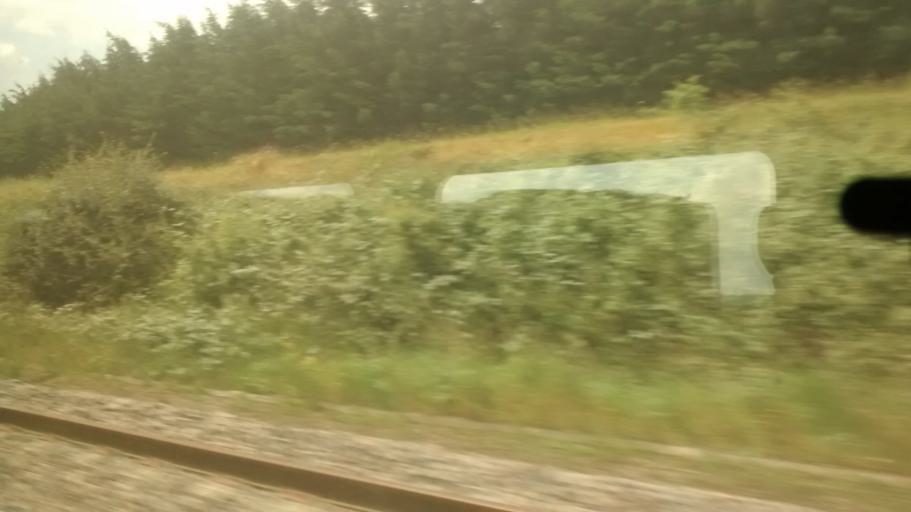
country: FR
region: Bourgogne
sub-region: Departement de Saone-et-Loire
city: Epinac
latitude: 46.9996
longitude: 4.4521
